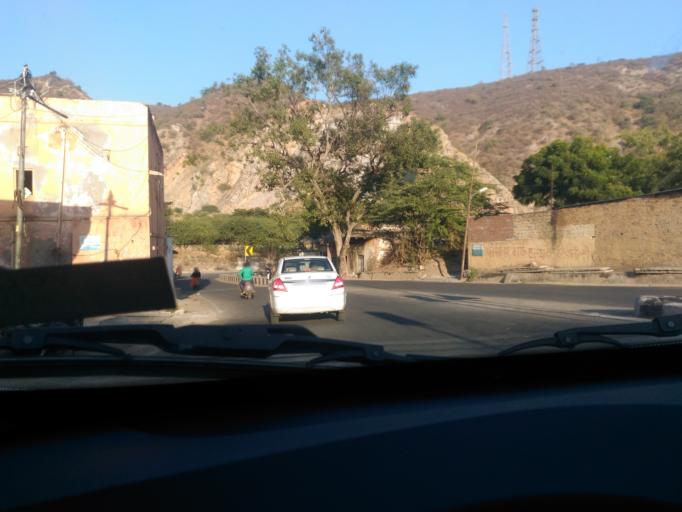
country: IN
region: Rajasthan
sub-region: Jaipur
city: Jaipur
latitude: 26.9018
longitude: 75.8505
